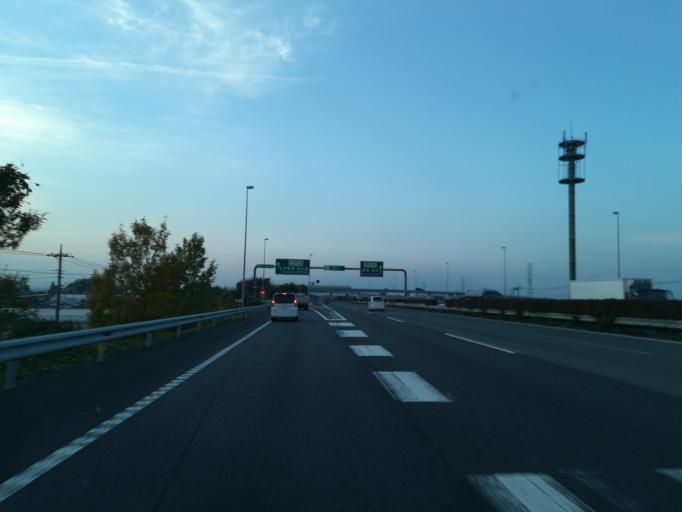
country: JP
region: Gunma
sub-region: Sawa-gun
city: Tamamura
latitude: 36.3184
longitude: 139.0795
